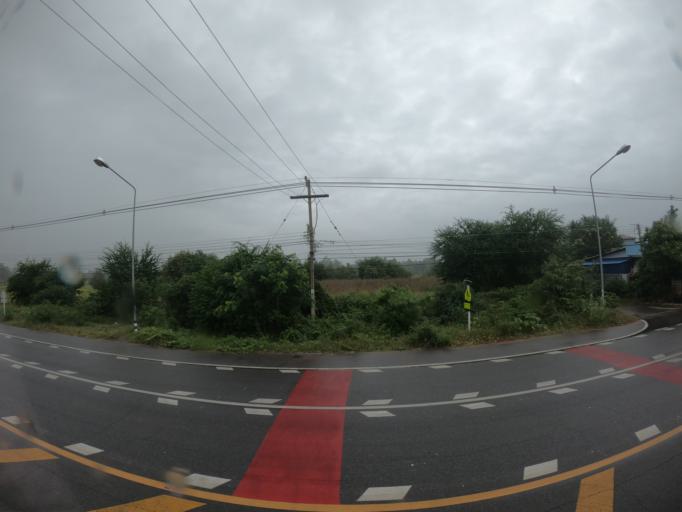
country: TH
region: Maha Sarakham
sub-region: Amphoe Borabue
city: Borabue
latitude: 16.0452
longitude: 103.1086
